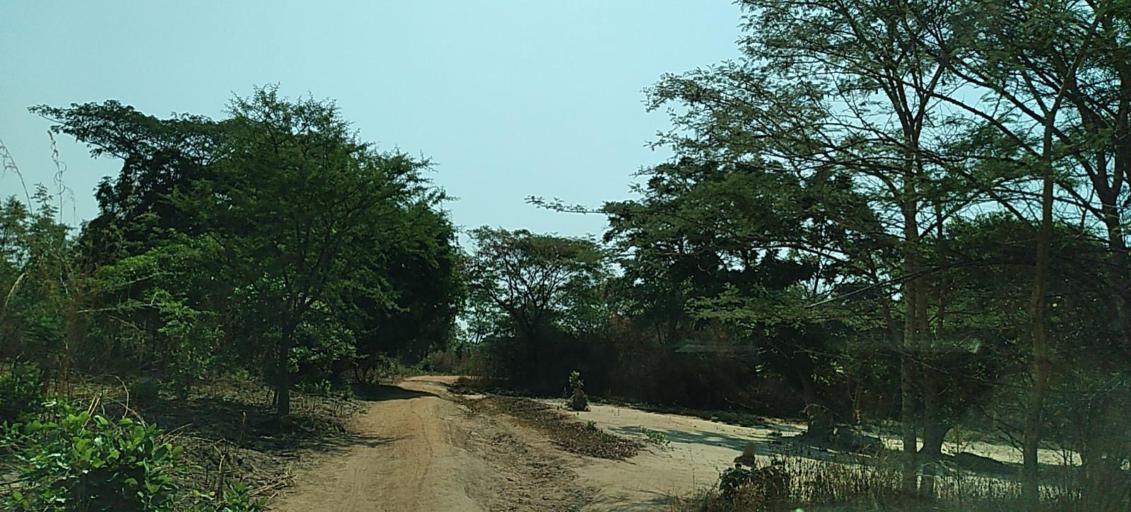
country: ZM
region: Copperbelt
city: Luanshya
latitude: -13.2810
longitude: 28.3149
